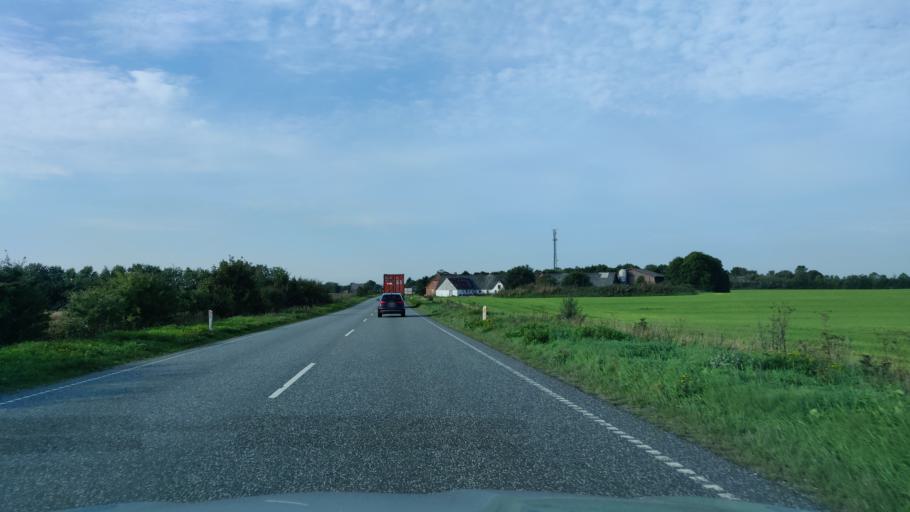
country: DK
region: North Denmark
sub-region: Vesthimmerland Kommune
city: Aars
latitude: 56.7762
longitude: 9.5762
